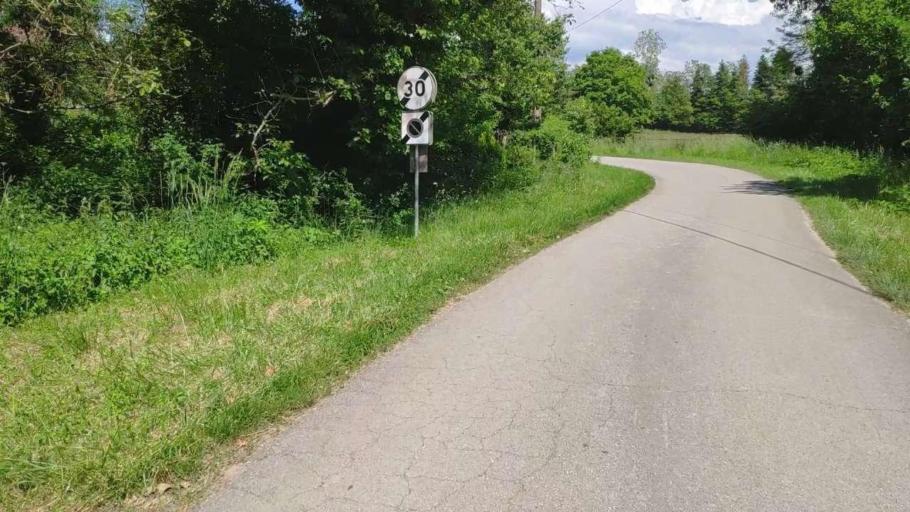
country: FR
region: Franche-Comte
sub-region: Departement du Jura
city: Bletterans
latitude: 46.7855
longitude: 5.3948
